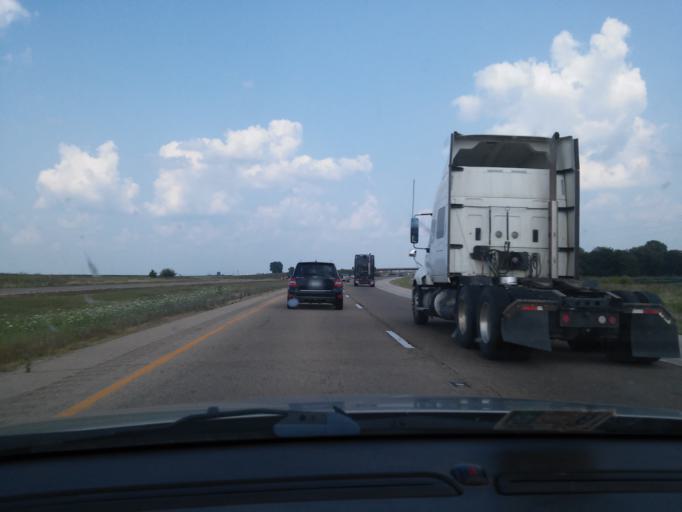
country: US
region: Illinois
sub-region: McLean County
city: Lexington
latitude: 40.6562
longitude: -88.7998
